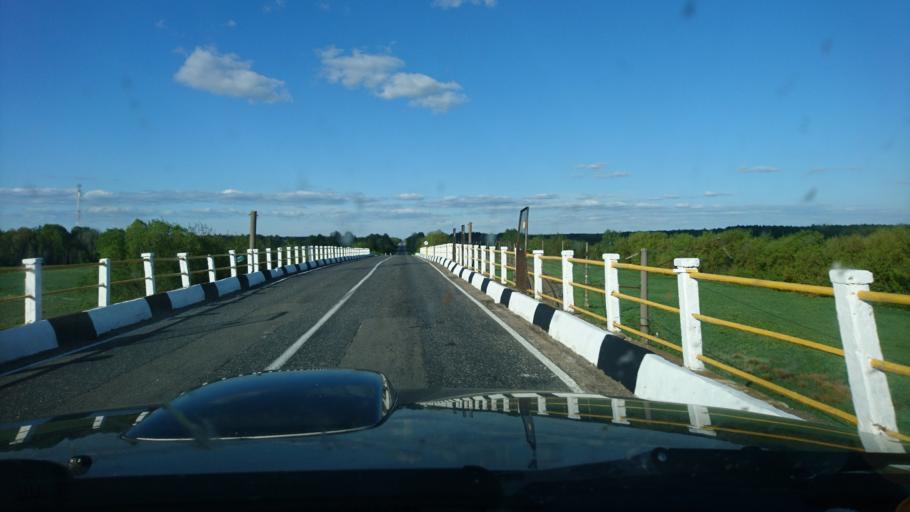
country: BY
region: Brest
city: Nyakhachava
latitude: 52.6389
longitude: 25.1952
